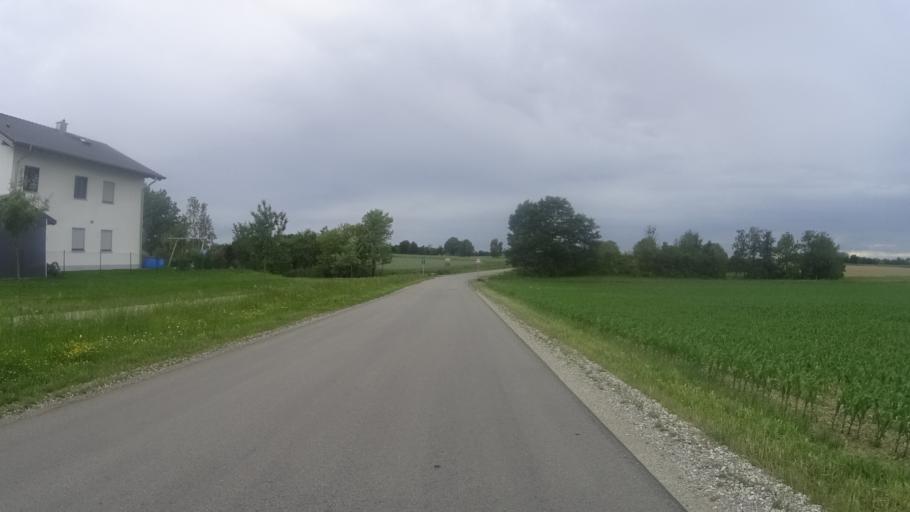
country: DE
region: Bavaria
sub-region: Upper Bavaria
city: Bockhorn
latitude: 48.3145
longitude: 11.9824
